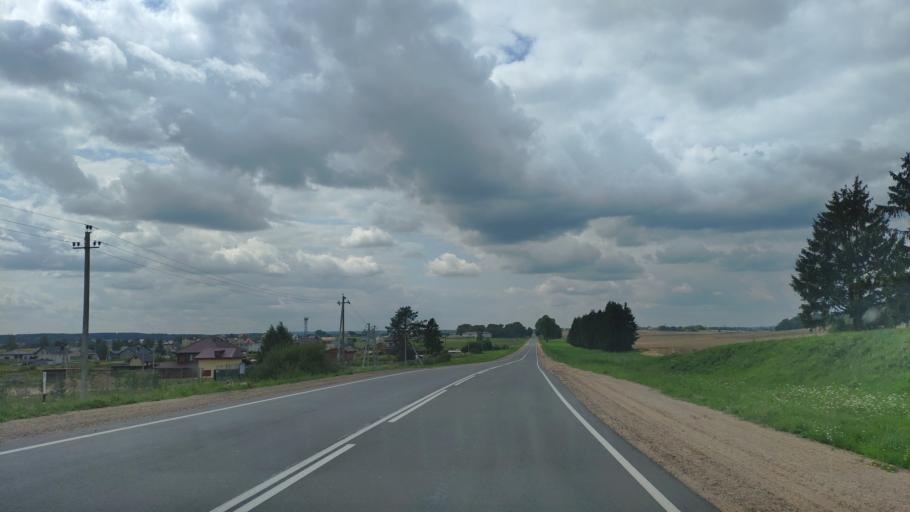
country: BY
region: Minsk
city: Zaslawye
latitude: 54.0051
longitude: 27.3515
